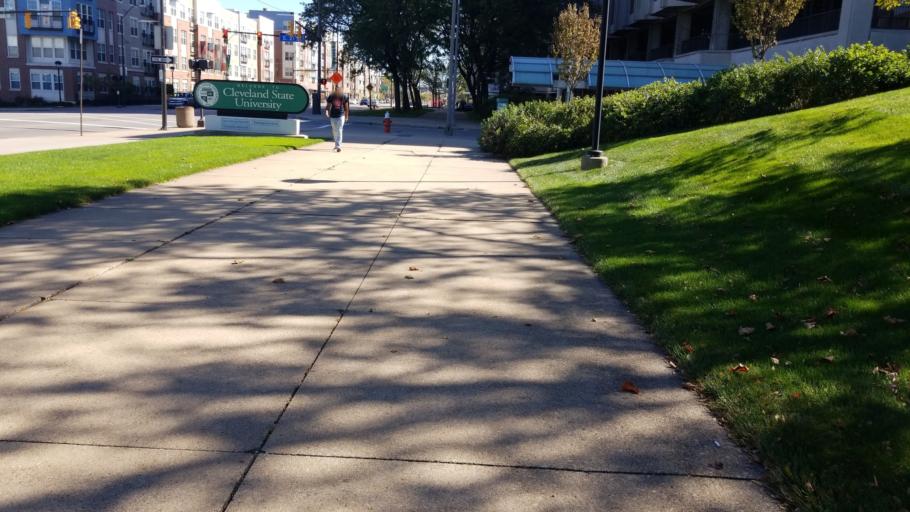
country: US
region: Ohio
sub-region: Cuyahoga County
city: Cleveland
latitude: 41.5034
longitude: -81.6767
